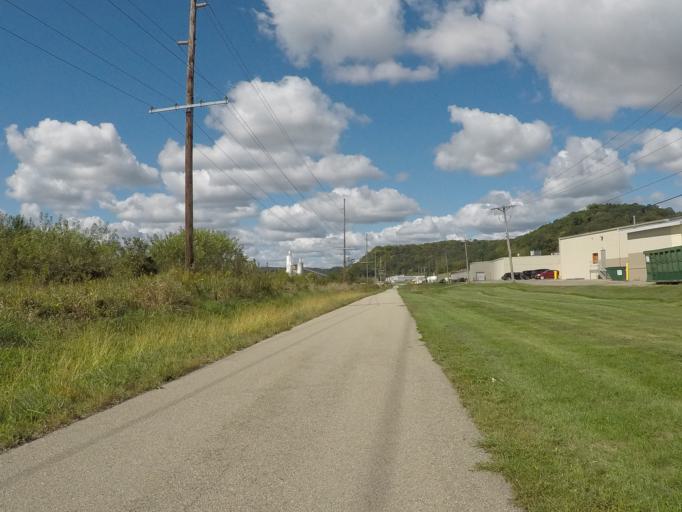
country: US
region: Wisconsin
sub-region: Richland County
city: Richland Center
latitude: 43.3162
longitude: -90.3604
